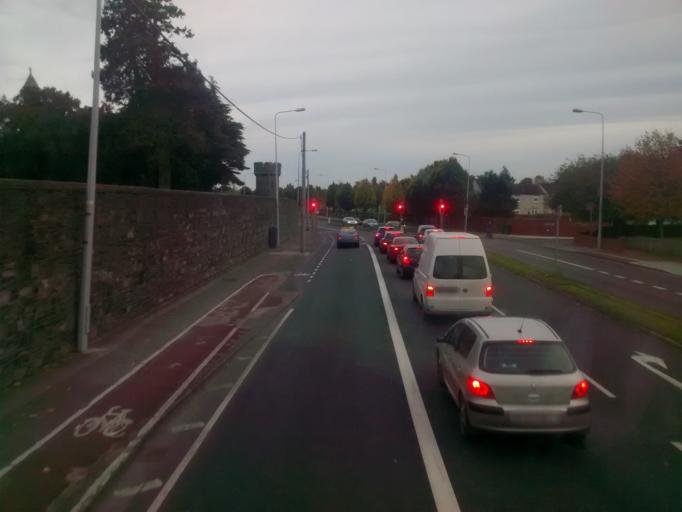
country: IE
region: Leinster
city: Cabra
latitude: 53.3713
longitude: -6.2807
